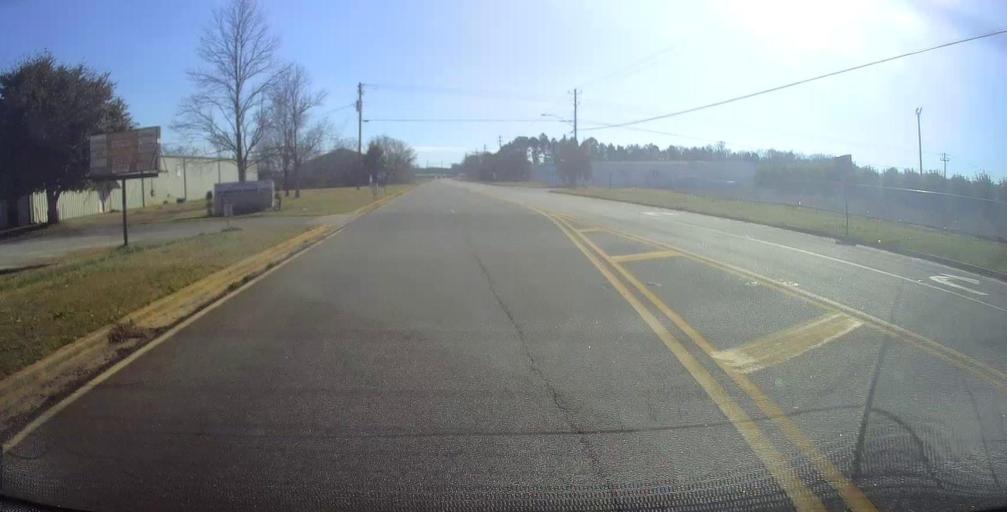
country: US
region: Georgia
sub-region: Sumter County
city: Americus
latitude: 32.1138
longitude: -84.1999
